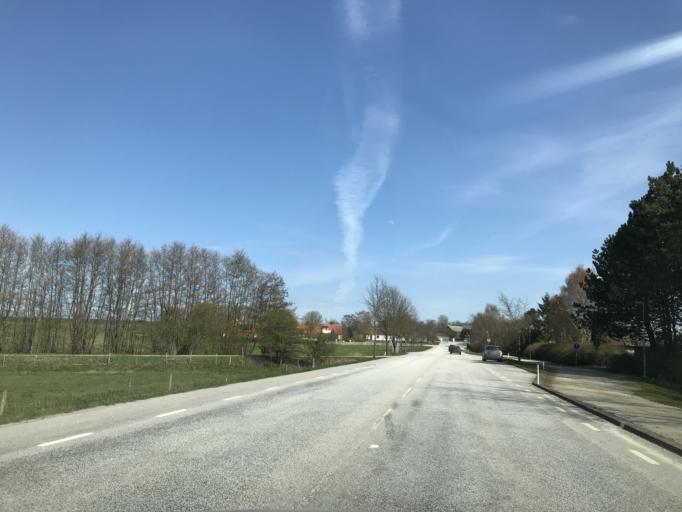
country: SE
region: Skane
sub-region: Eslovs Kommun
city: Eslov
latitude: 55.7649
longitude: 13.3176
